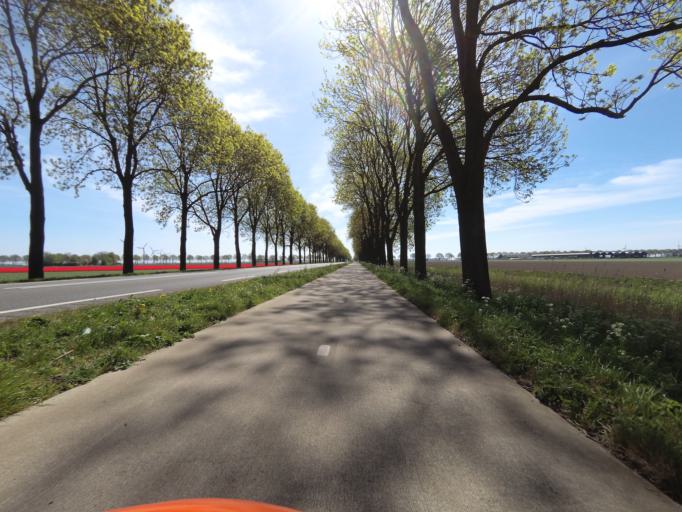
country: NL
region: Flevoland
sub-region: Gemeente Dronten
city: Biddinghuizen
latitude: 52.4868
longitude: 5.6594
